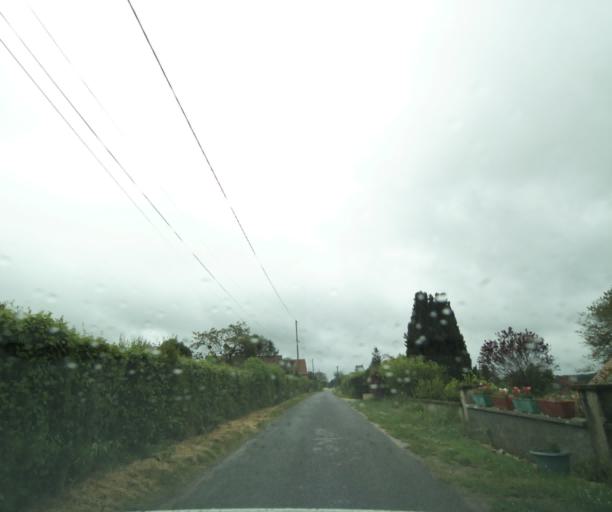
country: FR
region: Bourgogne
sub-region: Departement de Saone-et-Loire
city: Charolles
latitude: 46.4864
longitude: 4.4158
